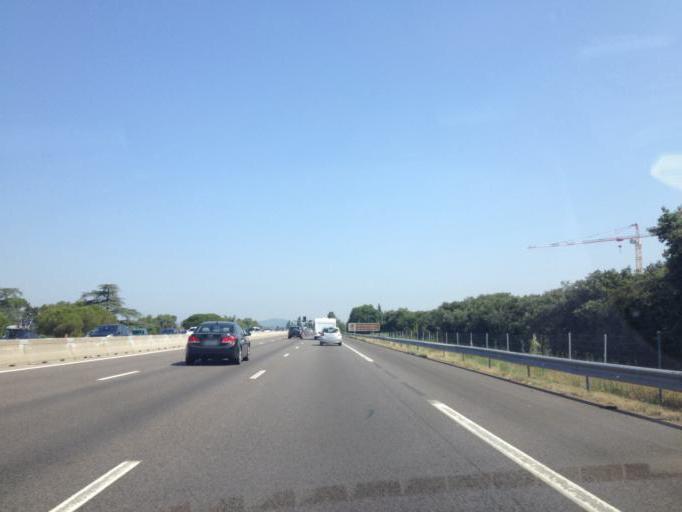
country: FR
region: Rhone-Alpes
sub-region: Departement de la Drome
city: Saint-Paul-Trois-Chateaux
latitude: 44.3499
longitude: 4.7380
